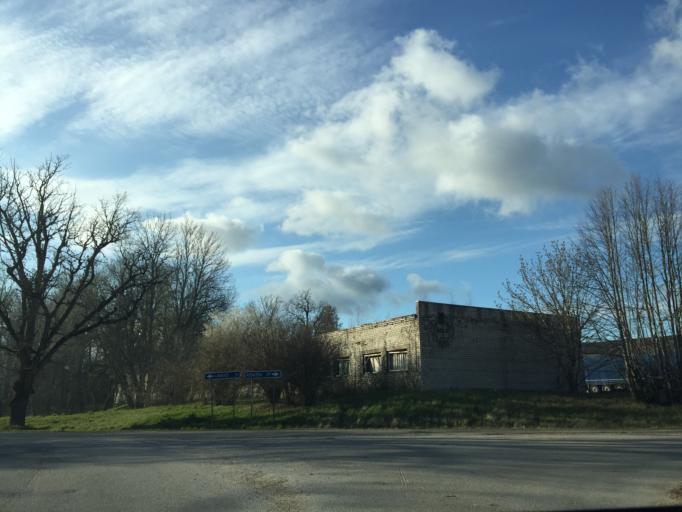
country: LV
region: Burtnieki
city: Matisi
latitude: 57.6359
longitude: 25.0502
